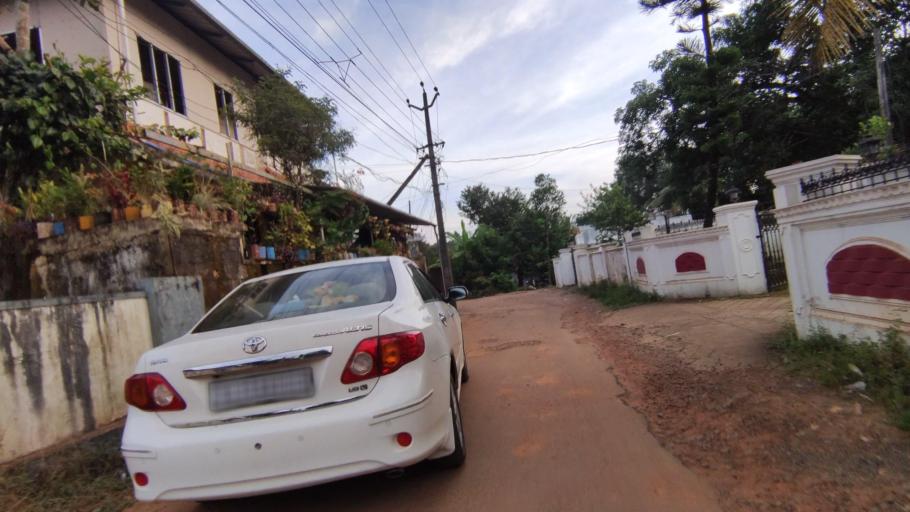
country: IN
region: Kerala
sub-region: Kottayam
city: Kottayam
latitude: 9.6361
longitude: 76.5043
